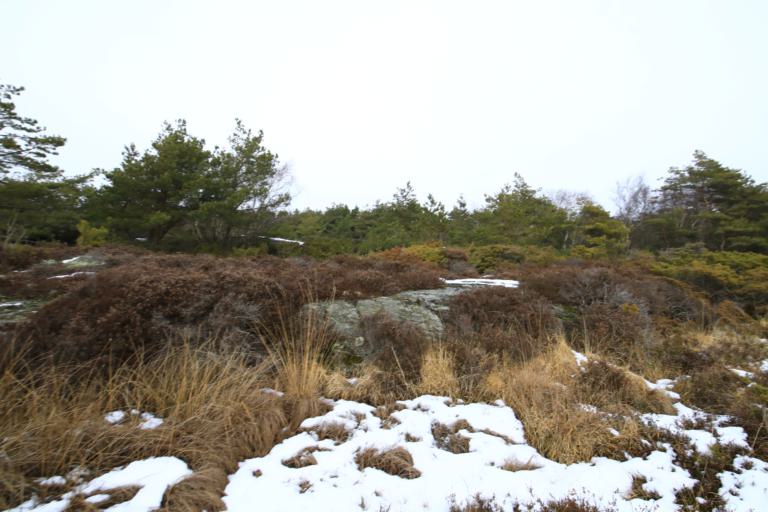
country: SE
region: Halland
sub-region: Kungsbacka Kommun
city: Frillesas
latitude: 57.2186
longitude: 12.1402
